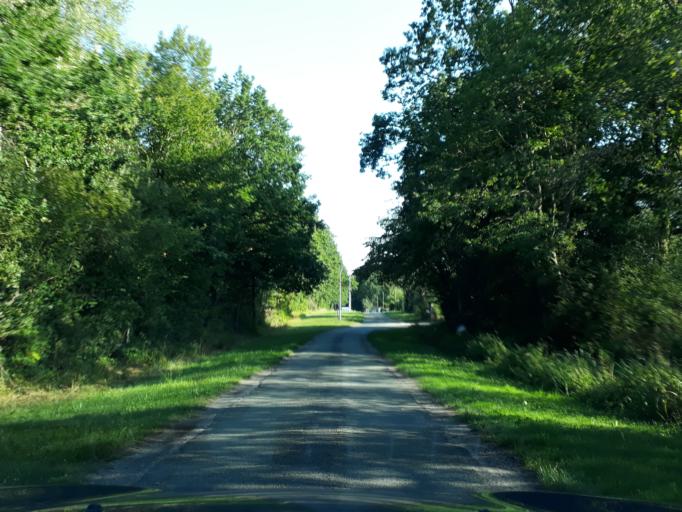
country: FR
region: Centre
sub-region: Departement du Loiret
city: Chaingy
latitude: 47.9290
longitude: 1.7428
